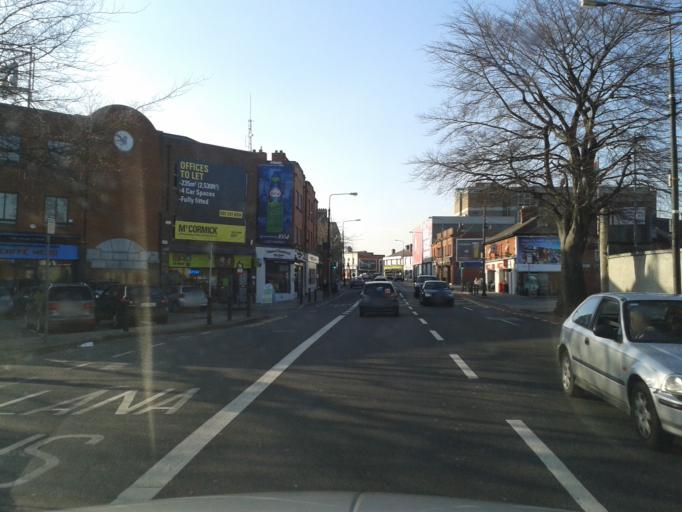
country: IE
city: Clonskeagh
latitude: 53.3208
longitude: -6.2342
